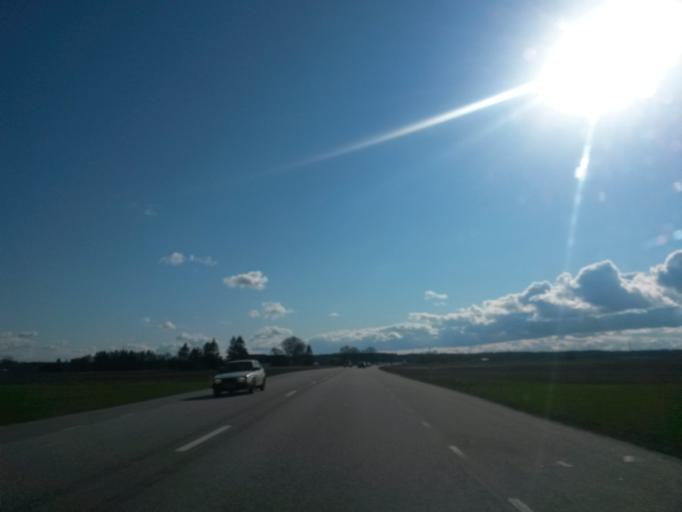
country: SE
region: Vaestra Goetaland
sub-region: Vara Kommun
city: Vara
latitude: 58.2406
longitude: 12.9400
